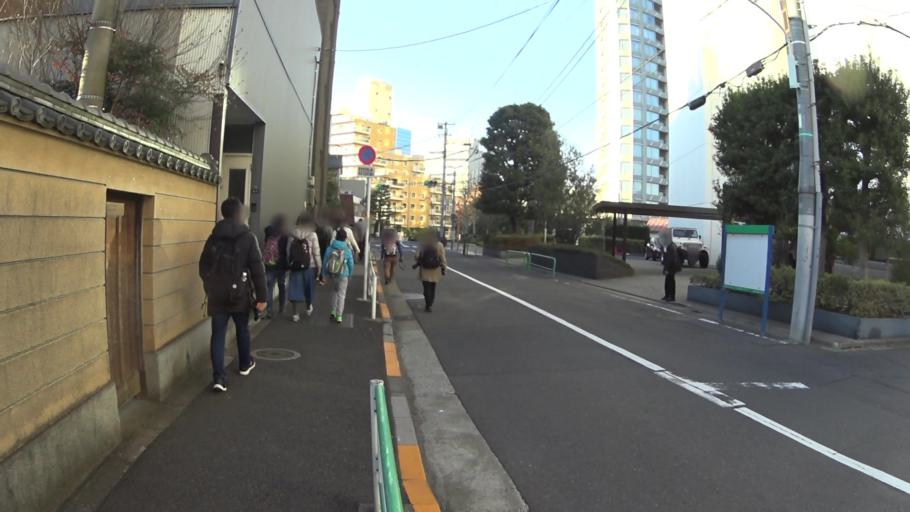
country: JP
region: Tokyo
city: Tokyo
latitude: 35.6725
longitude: 139.7321
